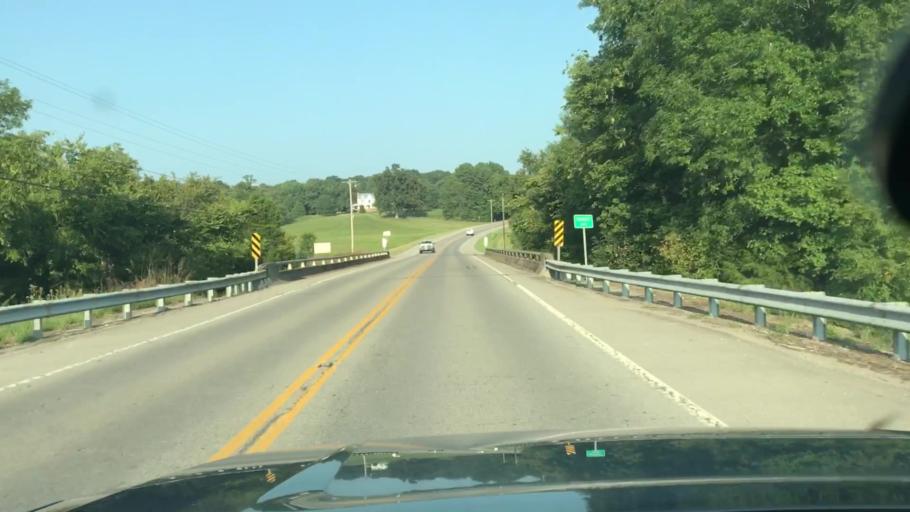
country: US
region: Tennessee
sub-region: Sumner County
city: Portland
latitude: 36.5786
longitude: -86.4584
